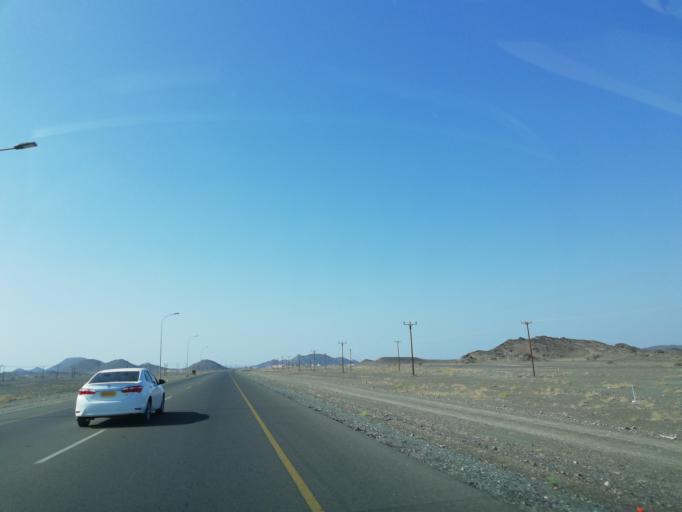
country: OM
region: Ash Sharqiyah
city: Ibra'
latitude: 22.7440
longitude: 58.1494
